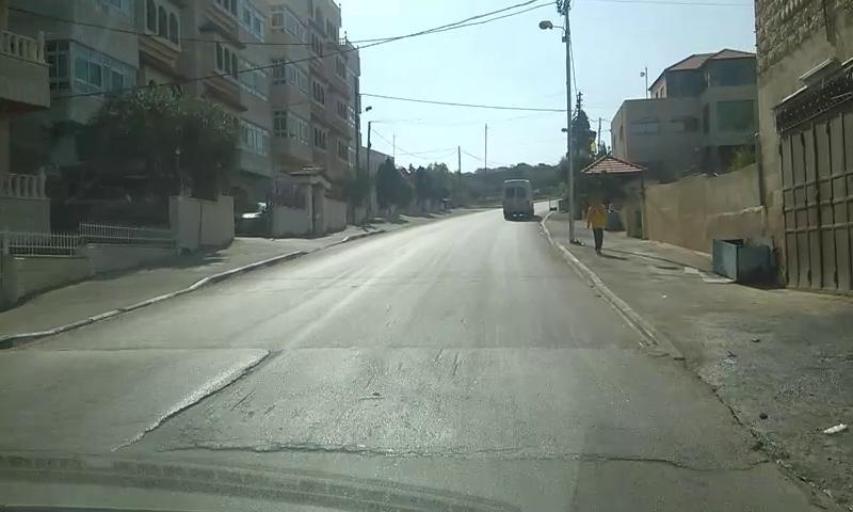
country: PS
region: West Bank
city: At Taybah
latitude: 31.9599
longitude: 35.2968
